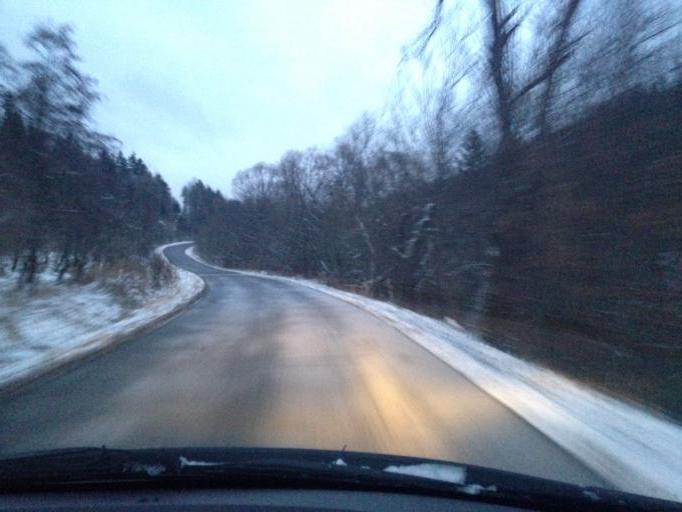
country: PL
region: Subcarpathian Voivodeship
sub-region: Powiat jasielski
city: Krempna
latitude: 49.5096
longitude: 21.5413
